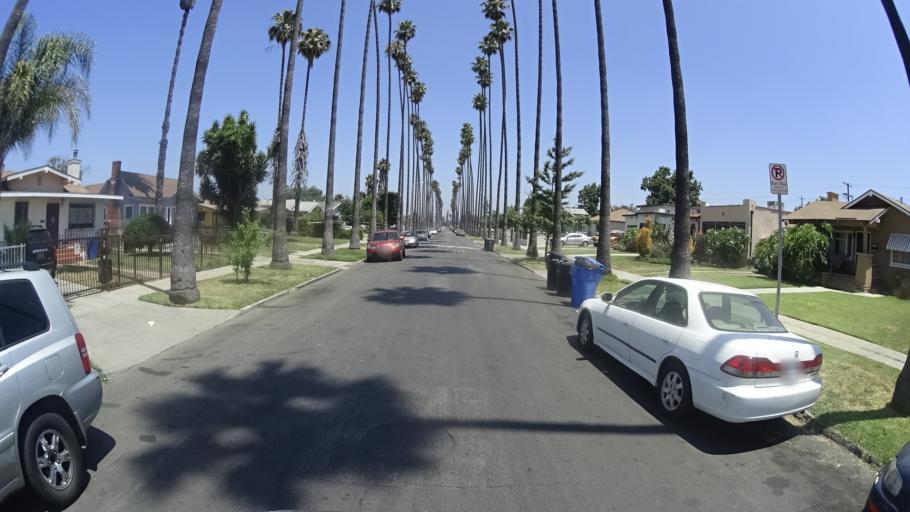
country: US
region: California
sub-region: Los Angeles County
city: View Park-Windsor Hills
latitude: 33.9981
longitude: -118.3204
